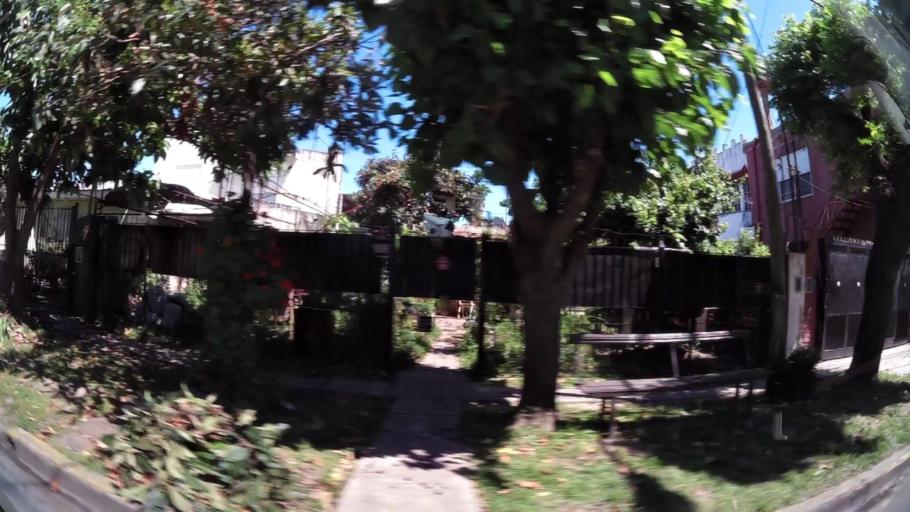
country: AR
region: Buenos Aires
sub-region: Partido de Tigre
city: Tigre
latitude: -34.4988
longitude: -58.6165
